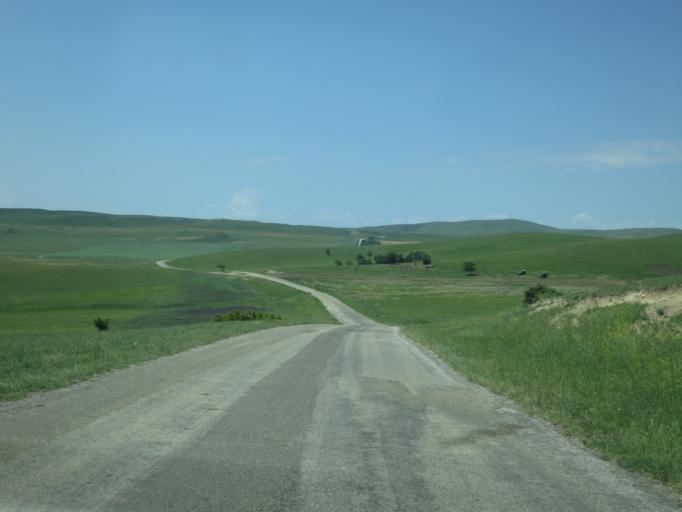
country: GE
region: Kakheti
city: Sagarejo
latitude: 41.6046
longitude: 45.3407
